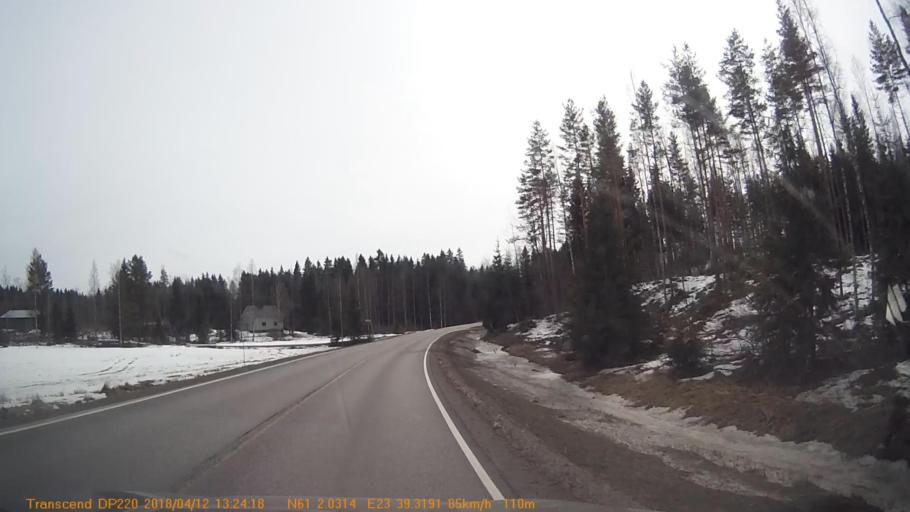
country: FI
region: Pirkanmaa
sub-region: Etelae-Pirkanmaa
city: Kylmaekoski
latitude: 61.0327
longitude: 23.6557
